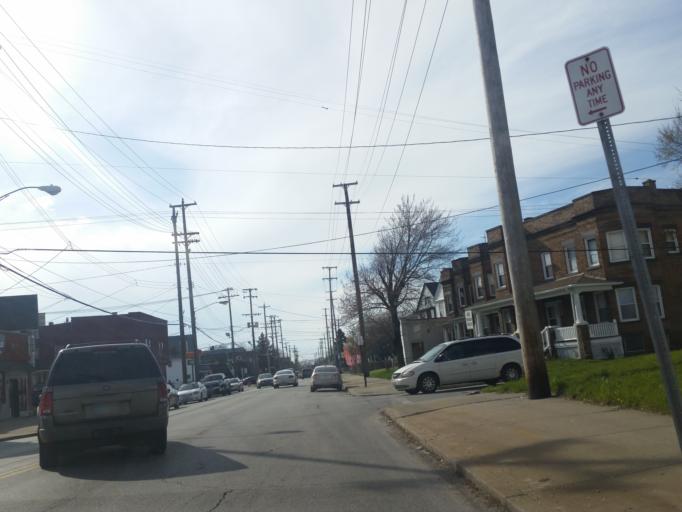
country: US
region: Ohio
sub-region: Cuyahoga County
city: Brooklyn
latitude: 41.4645
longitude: -81.7455
